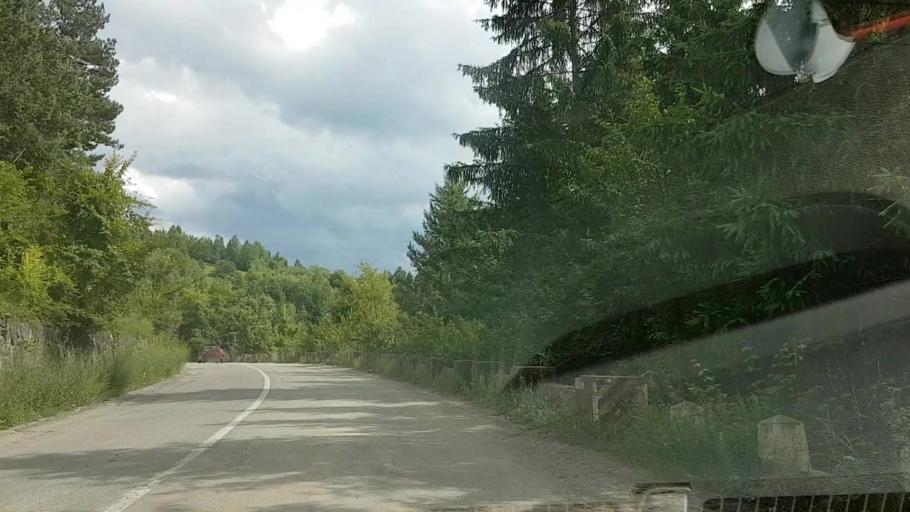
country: RO
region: Neamt
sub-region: Comuna Hangu
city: Hangu
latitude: 47.0521
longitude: 26.0386
